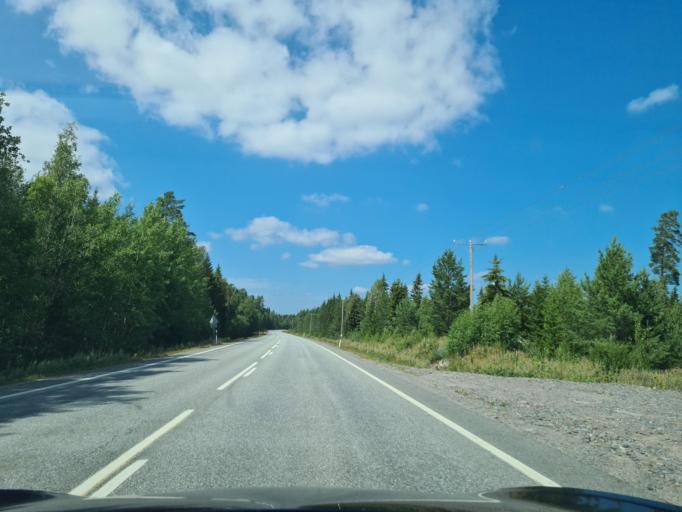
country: FI
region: Ostrobothnia
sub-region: Vaasa
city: Vaasa
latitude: 63.1687
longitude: 21.5864
